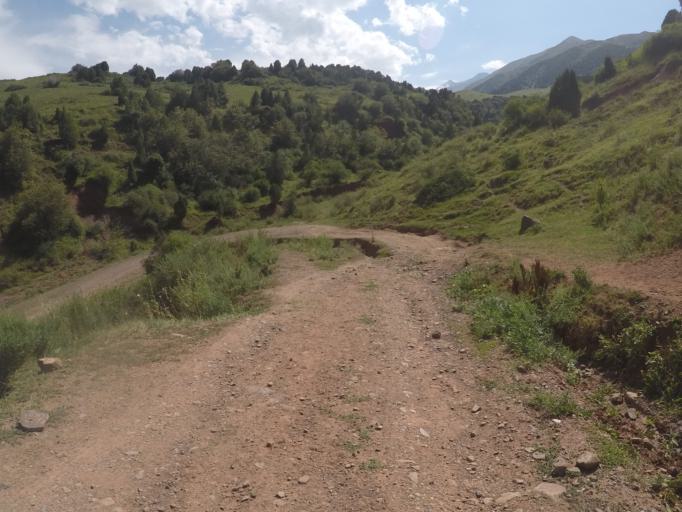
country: KG
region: Chuy
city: Bishkek
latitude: 42.6427
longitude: 74.6039
